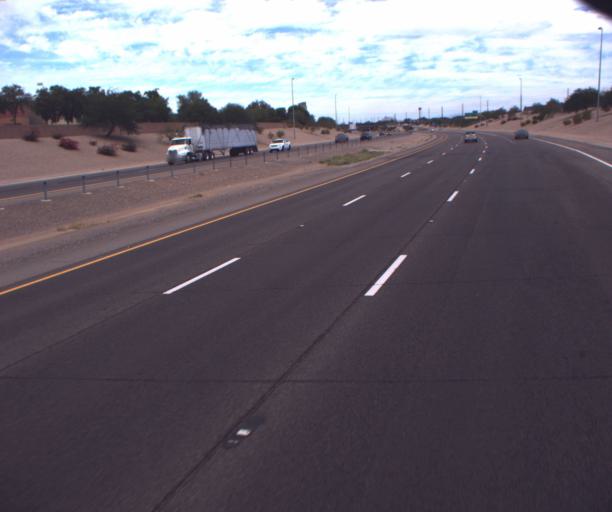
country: US
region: Arizona
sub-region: Maricopa County
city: Gilbert
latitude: 33.2996
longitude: -111.7401
